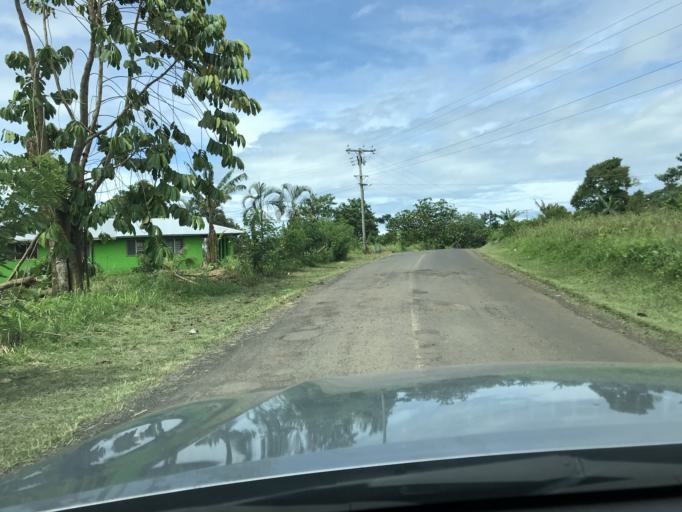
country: WS
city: Fasito`outa
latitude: -13.8595
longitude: -171.9088
